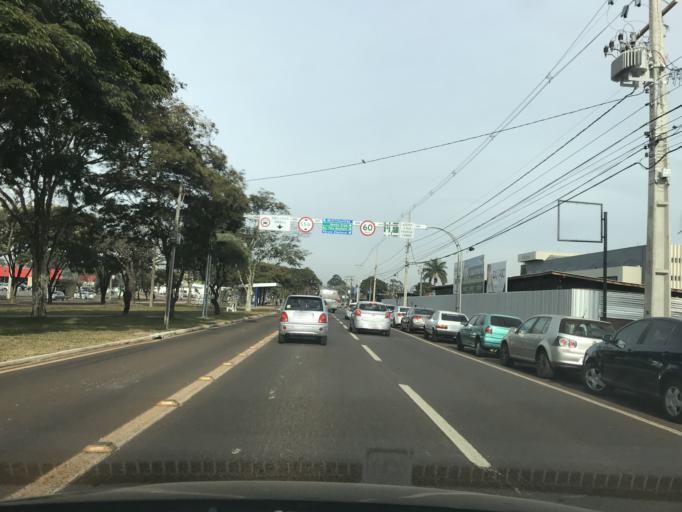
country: BR
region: Parana
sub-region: Cascavel
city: Cascavel
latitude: -24.9693
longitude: -53.4865
